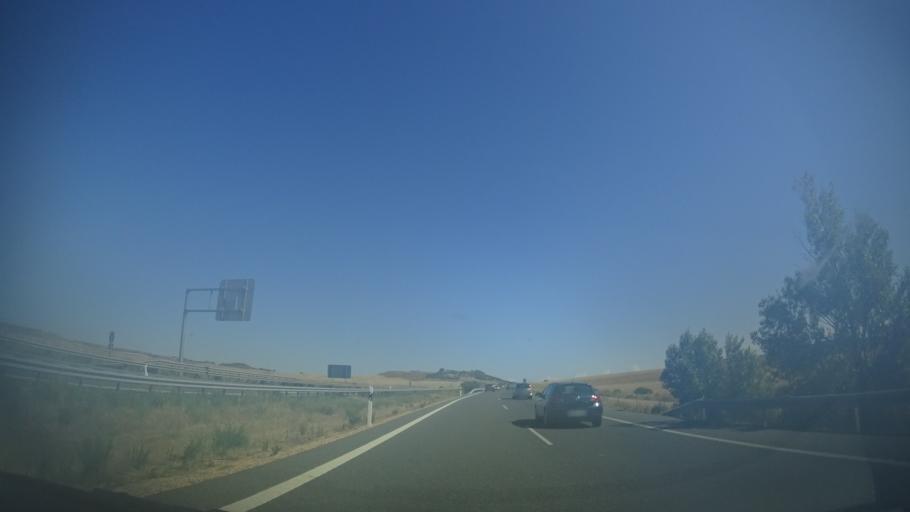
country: ES
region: Castille and Leon
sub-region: Provincia de Valladolid
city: Mota del Marques
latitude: 41.6227
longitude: -5.1646
